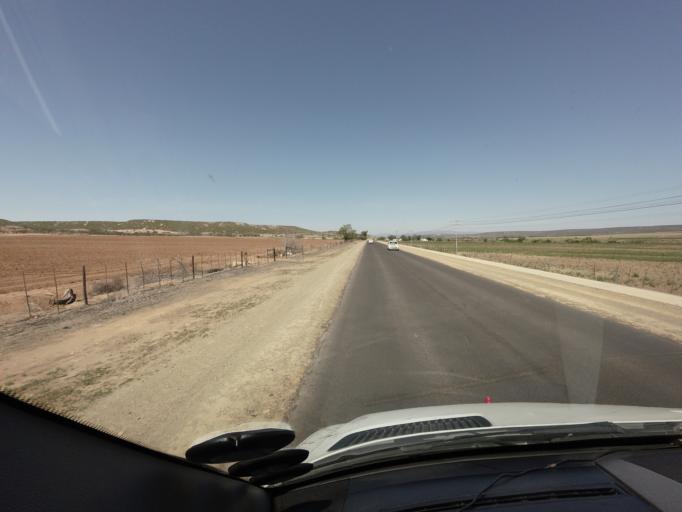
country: ZA
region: Western Cape
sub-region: Eden District Municipality
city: Oudtshoorn
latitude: -33.5532
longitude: 22.2317
